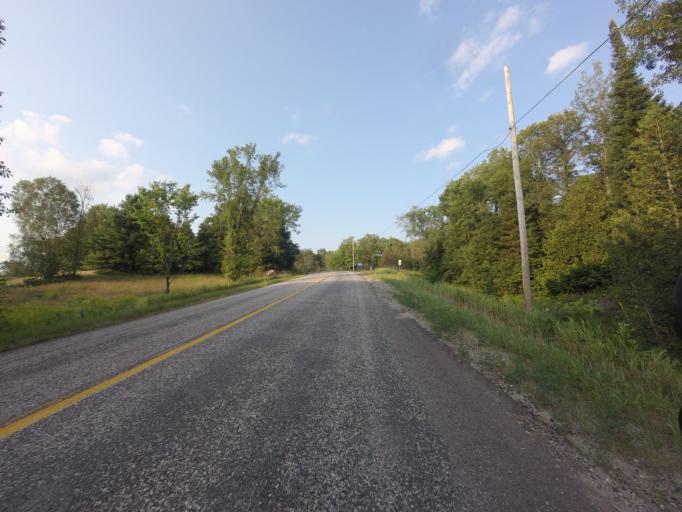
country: CA
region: Ontario
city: Renfrew
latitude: 44.9868
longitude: -76.7395
